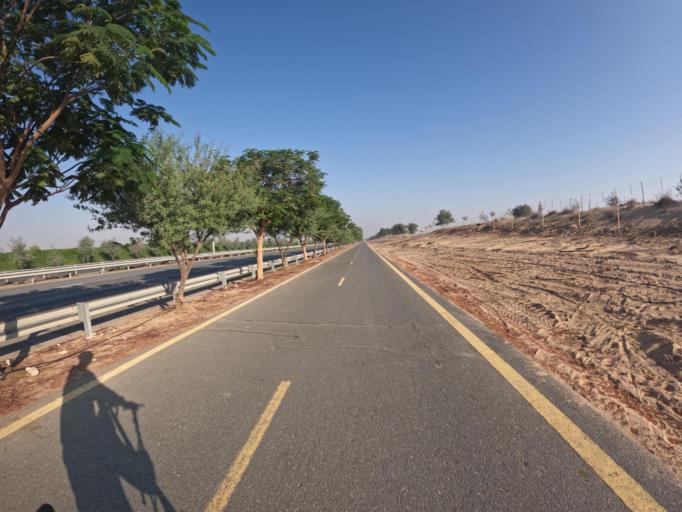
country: AE
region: Dubai
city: Dubai
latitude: 24.8679
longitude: 55.3407
